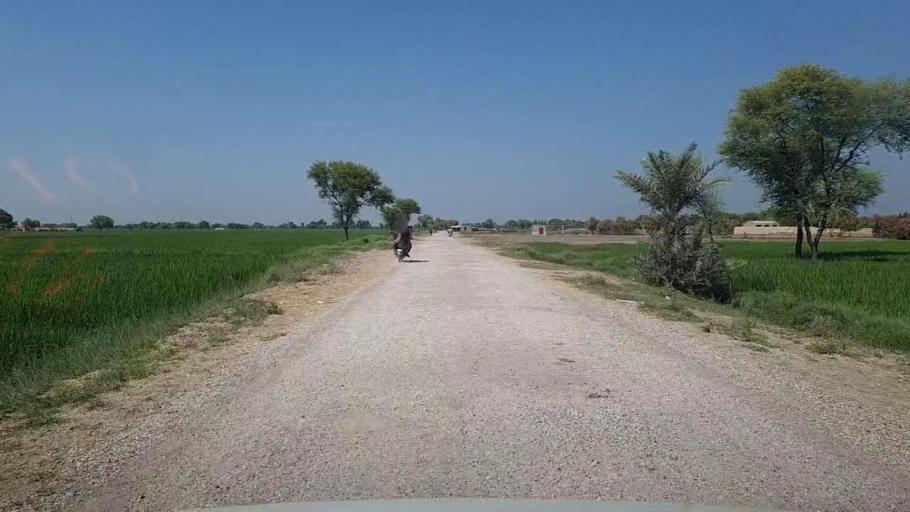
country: PK
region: Sindh
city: Kandhkot
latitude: 28.3220
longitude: 69.3664
